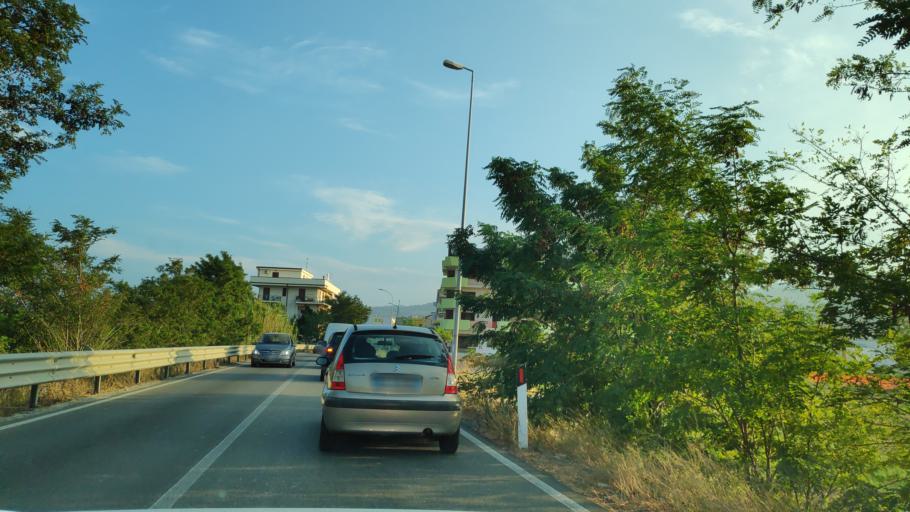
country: IT
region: Calabria
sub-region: Provincia di Catanzaro
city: Marina di Davoli
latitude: 38.6704
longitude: 16.5478
